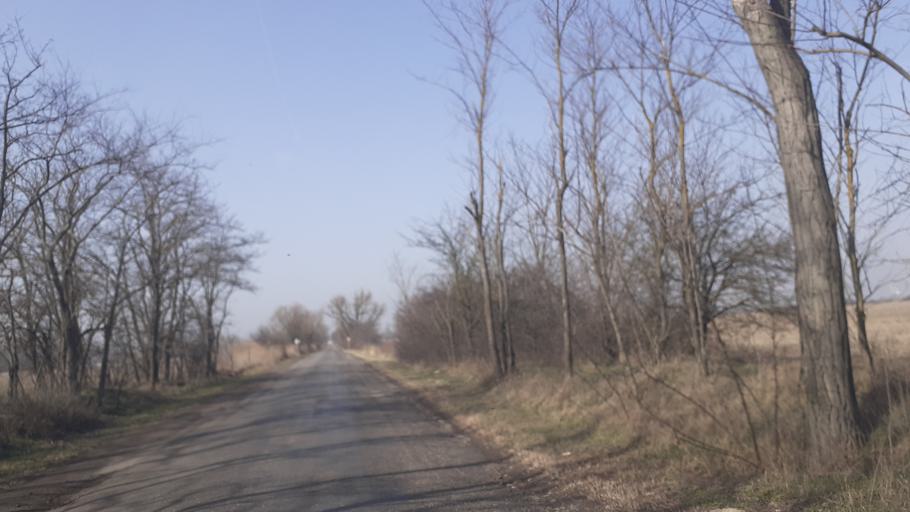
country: HU
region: Pest
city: Dabas
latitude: 47.0587
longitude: 19.2952
